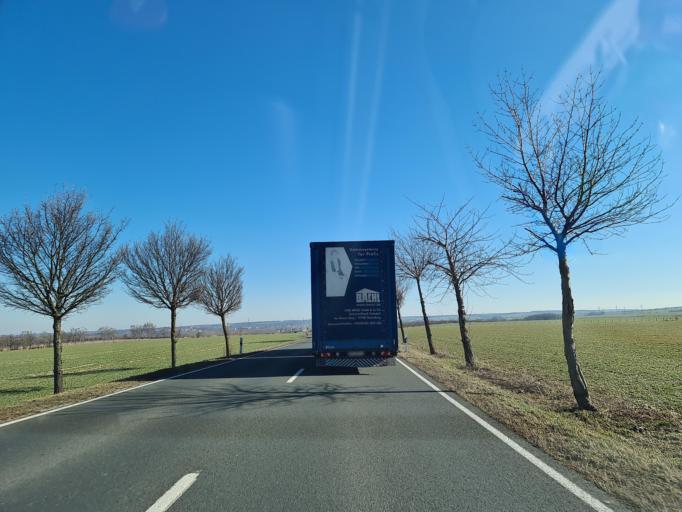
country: DE
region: Saxony-Anhalt
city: Droyssig
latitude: 51.0707
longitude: 12.0413
